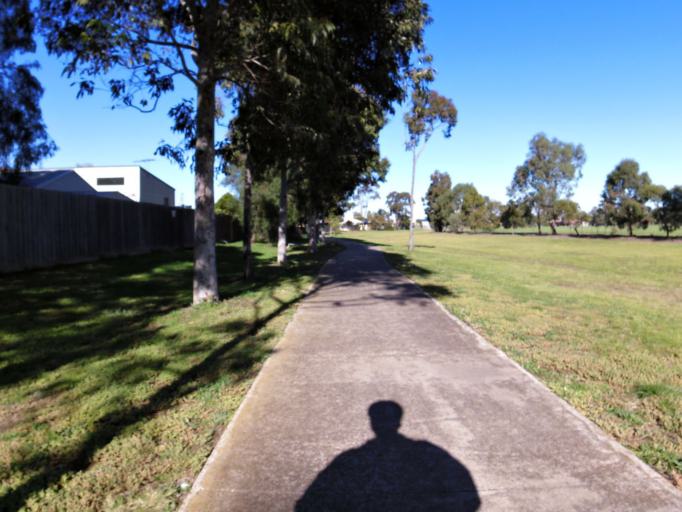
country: AU
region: Victoria
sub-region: Wyndham
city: Tarneit
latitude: -37.8695
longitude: 144.6773
